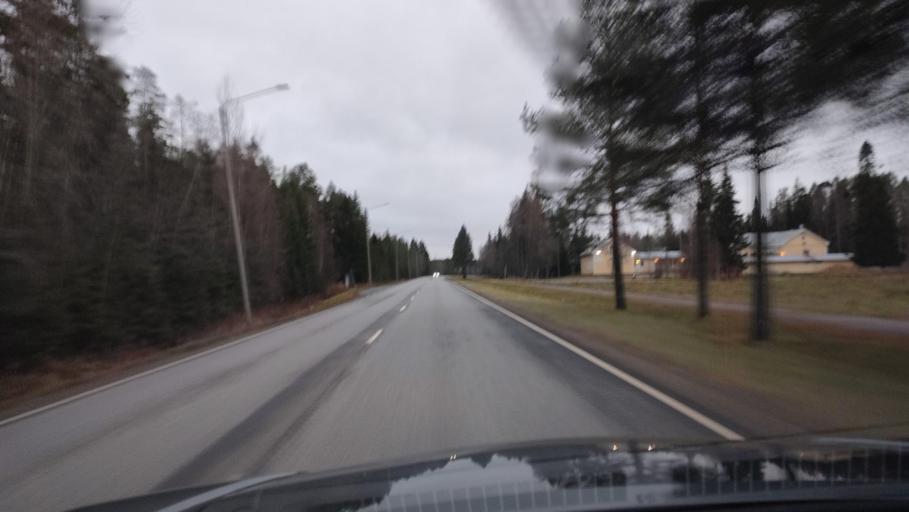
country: FI
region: Southern Ostrobothnia
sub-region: Suupohja
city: Kauhajoki
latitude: 62.3992
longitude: 22.1583
